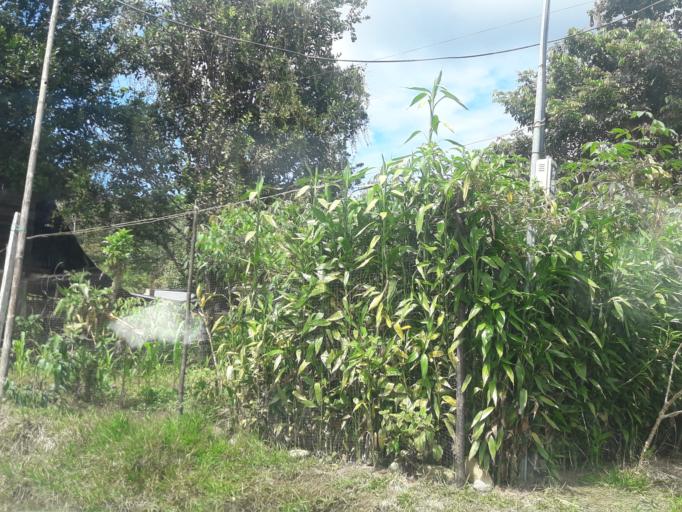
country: EC
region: Napo
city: Tena
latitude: -1.0175
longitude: -77.8614
